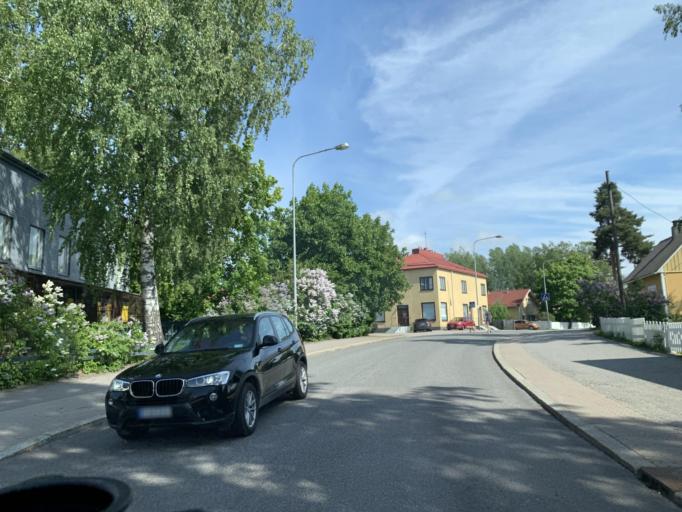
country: FI
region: Uusimaa
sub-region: Helsinki
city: Vantaa
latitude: 60.2607
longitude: 25.0202
